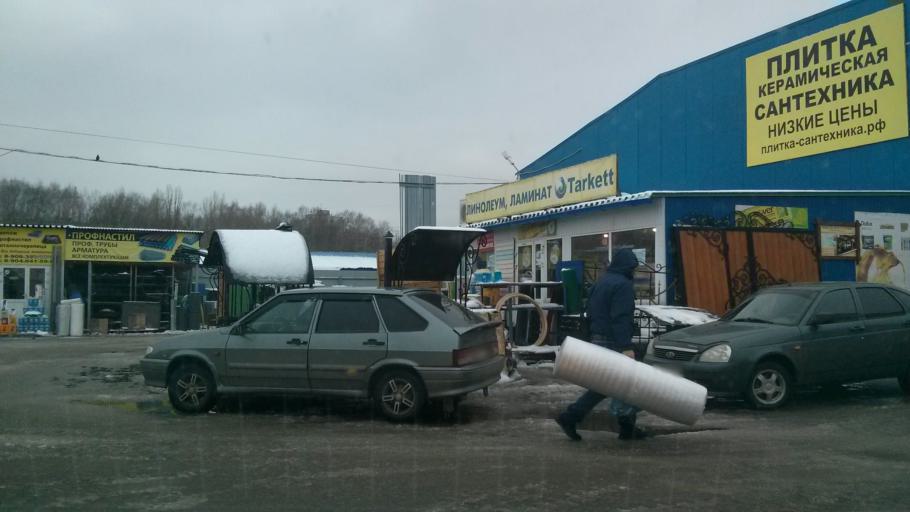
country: RU
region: Nizjnij Novgorod
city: Afonino
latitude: 56.2877
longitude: 44.0583
